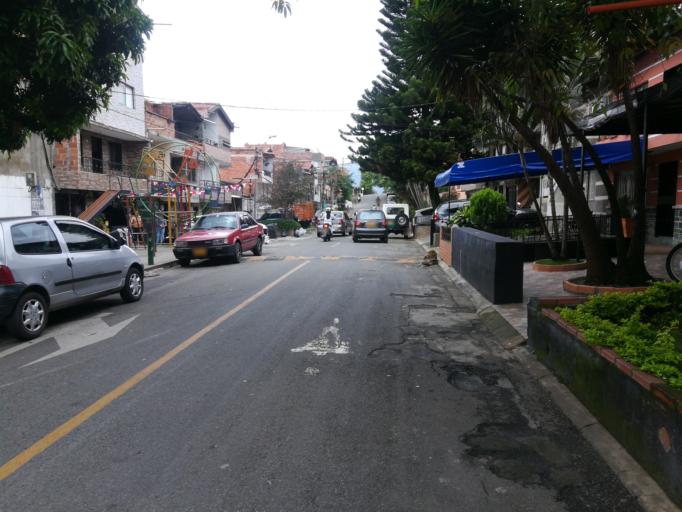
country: CO
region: Antioquia
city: Medellin
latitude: 6.2848
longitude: -75.5591
